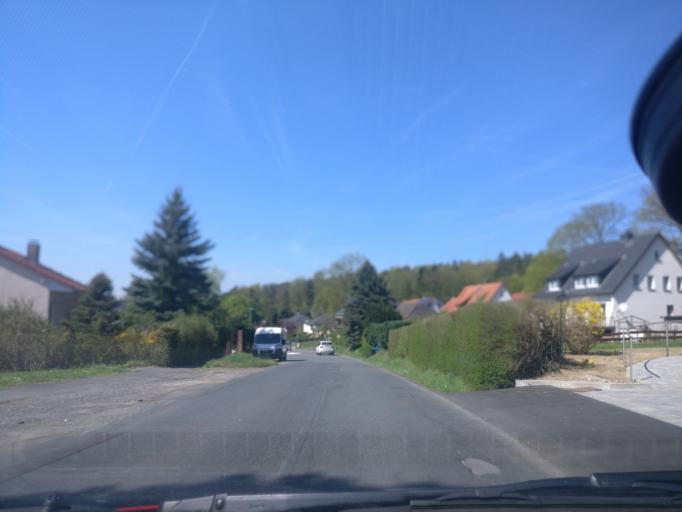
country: DE
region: Lower Saxony
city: Hannoversch Munden
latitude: 51.4055
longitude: 9.6690
